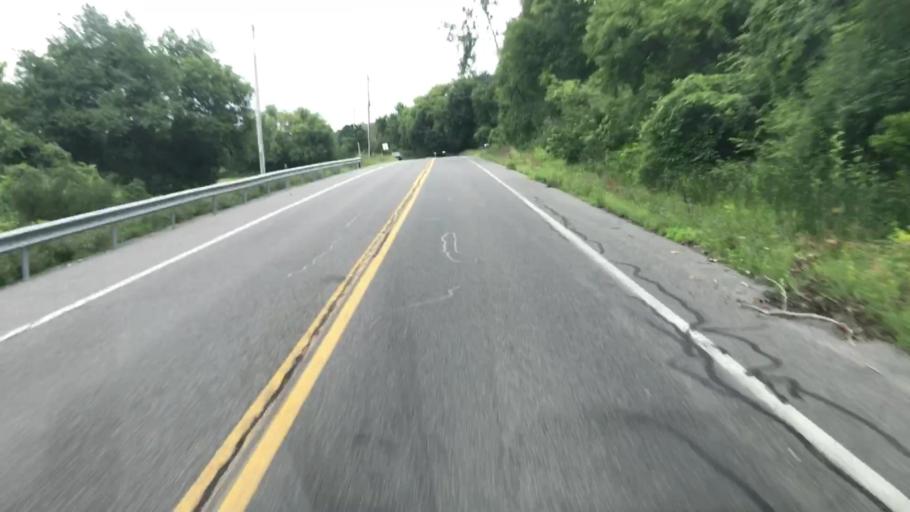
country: US
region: New York
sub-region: Onondaga County
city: Camillus
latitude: 43.0623
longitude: -76.3224
